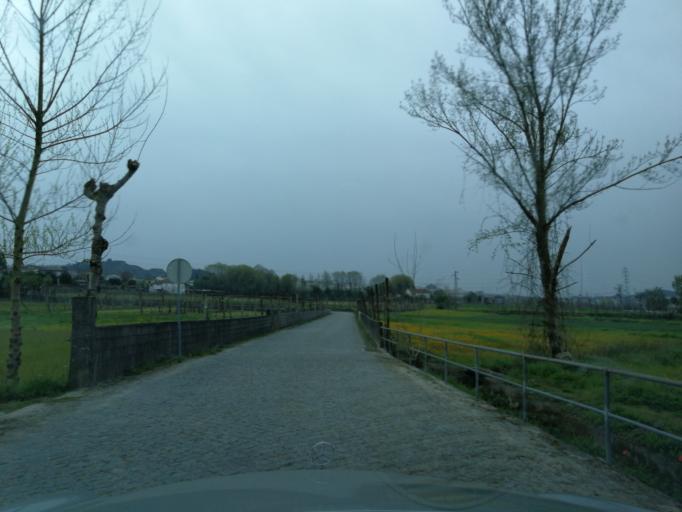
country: PT
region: Braga
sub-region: Braga
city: Braga
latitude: 41.5707
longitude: -8.4423
